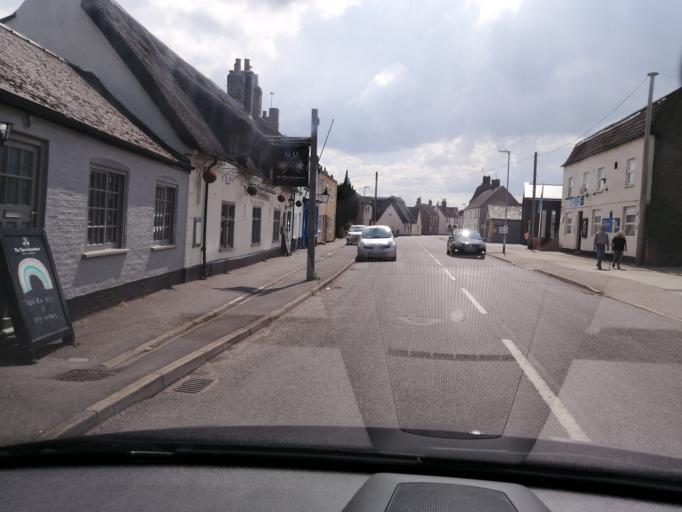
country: GB
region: England
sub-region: Cambridgeshire
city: Yaxley
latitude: 52.5122
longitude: -0.2604
